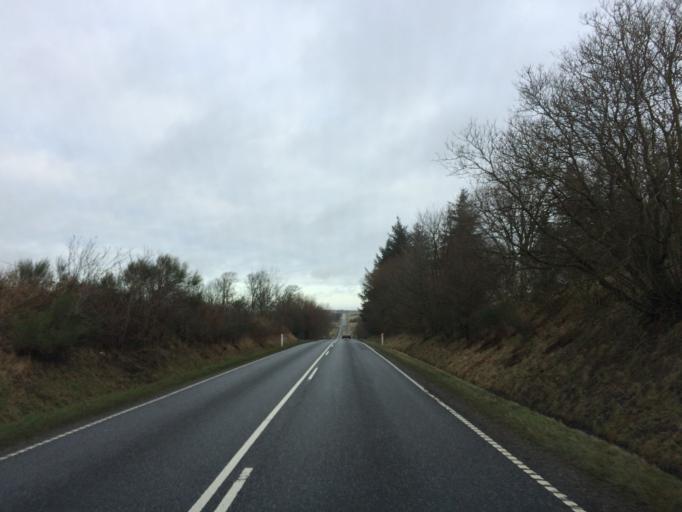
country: DK
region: Central Jutland
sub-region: Struer Kommune
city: Struer
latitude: 56.4274
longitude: 8.5101
